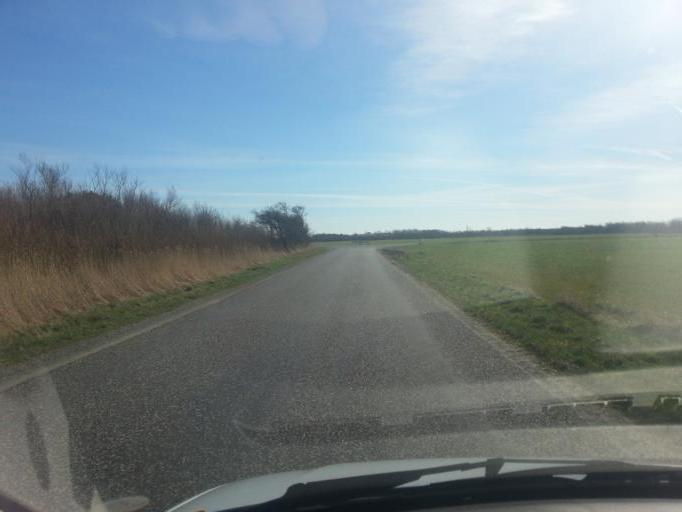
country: DK
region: South Denmark
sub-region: Esbjerg Kommune
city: Bramming
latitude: 55.4612
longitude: 8.6529
